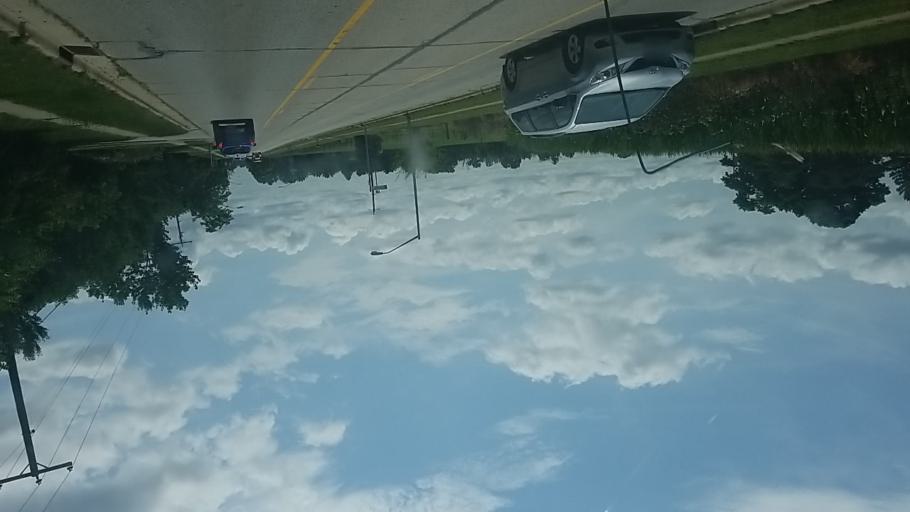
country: US
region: Ohio
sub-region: Franklin County
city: Reynoldsburg
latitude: 39.9636
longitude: -82.7709
